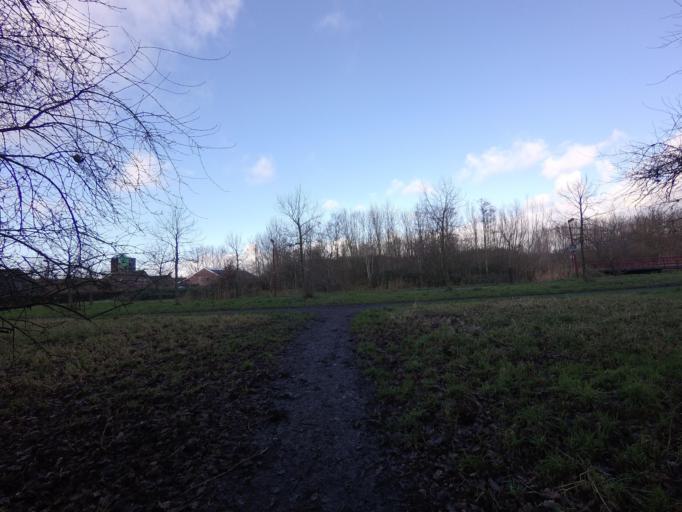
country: NL
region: Utrecht
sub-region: Gemeente Nieuwegein
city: Nieuwegein
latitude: 52.0571
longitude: 5.0707
